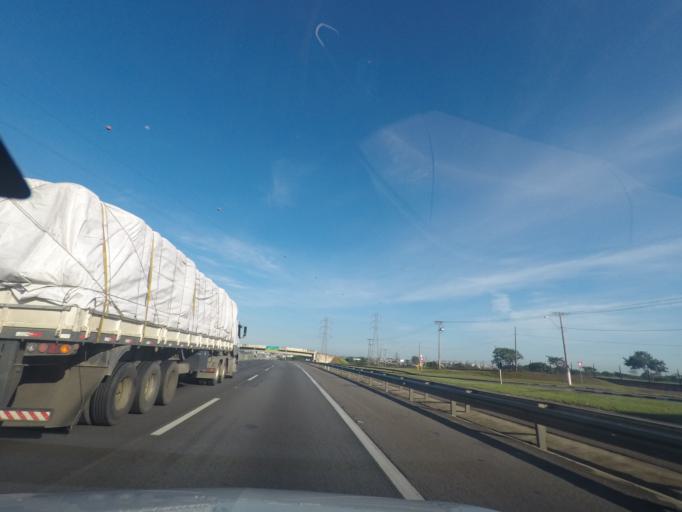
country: BR
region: Sao Paulo
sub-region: Hortolandia
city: Hortolandia
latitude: -22.8284
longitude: -47.1820
